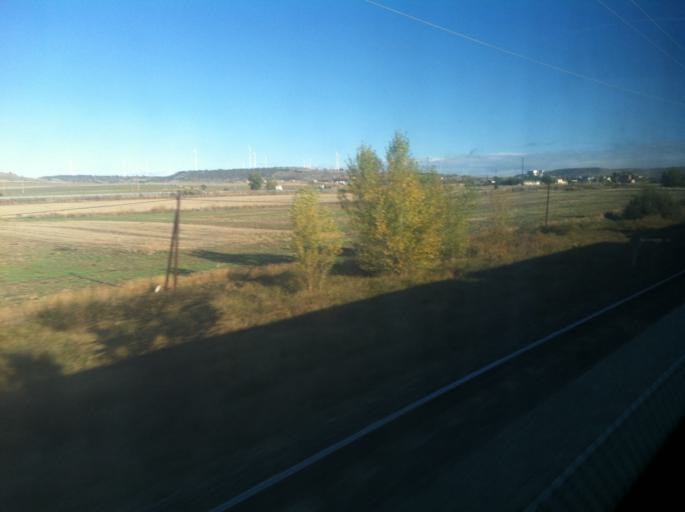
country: ES
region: Castille and Leon
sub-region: Provincia de Burgos
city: Villazopeque
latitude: 42.2100
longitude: -4.0060
